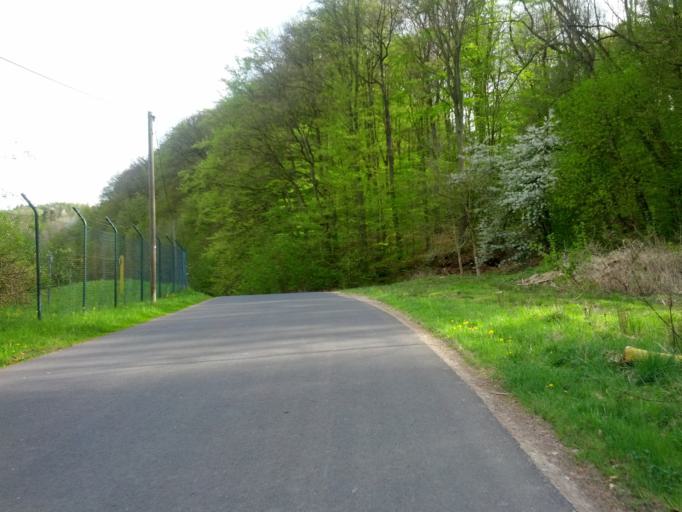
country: DE
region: Thuringia
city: Krauthausen
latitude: 50.9988
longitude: 10.2393
